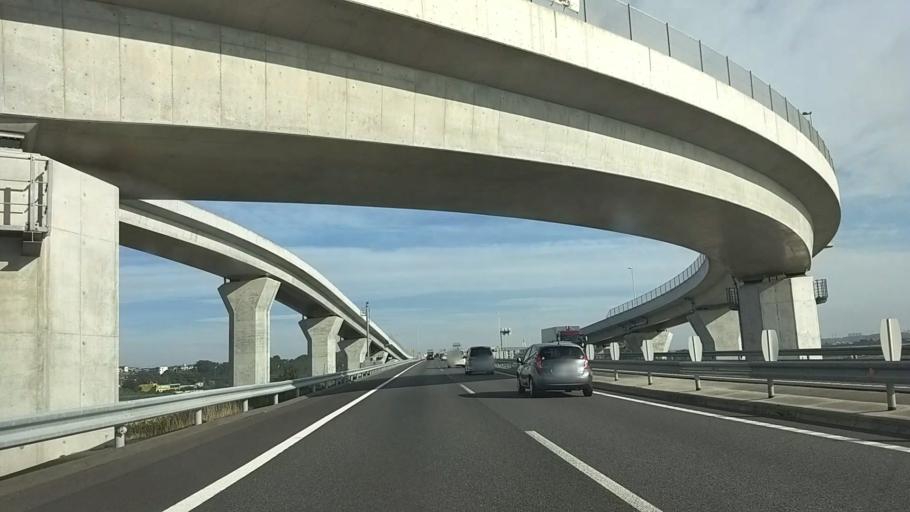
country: JP
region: Kanagawa
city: Zama
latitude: 35.4799
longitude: 139.3728
